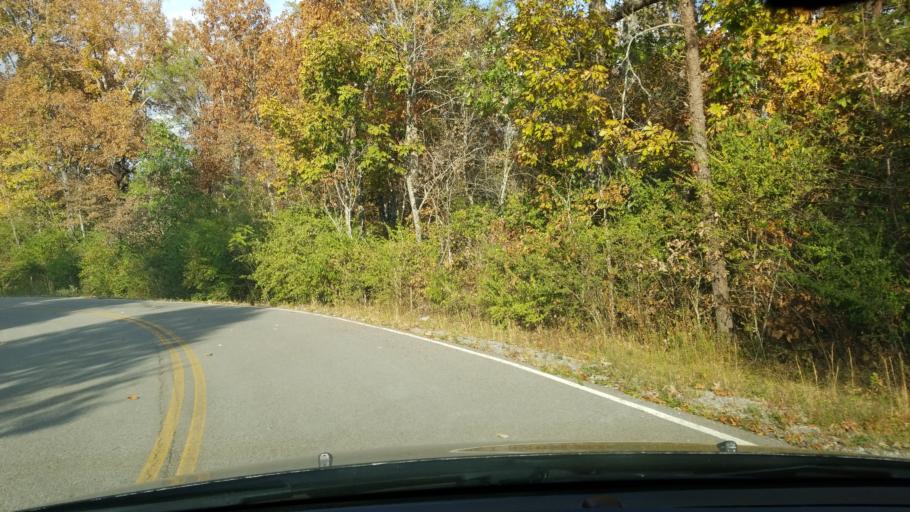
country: US
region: Tennessee
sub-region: Cumberland County
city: Crossville
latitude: 35.9485
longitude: -85.0495
